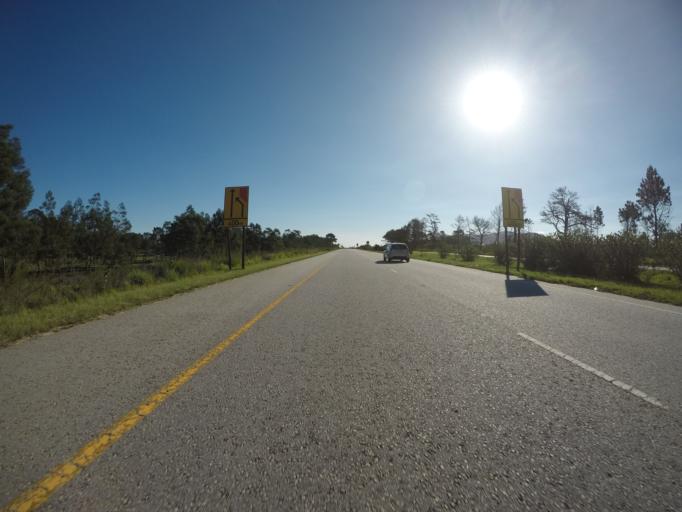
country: ZA
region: Eastern Cape
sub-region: Nelson Mandela Bay Metropolitan Municipality
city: Uitenhage
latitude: -33.9230
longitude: 25.3099
